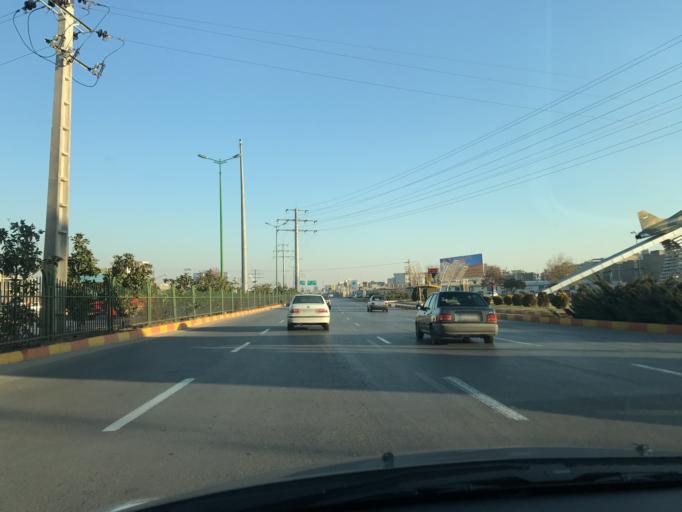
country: IR
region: Qazvin
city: Qazvin
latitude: 36.2873
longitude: 50.0104
